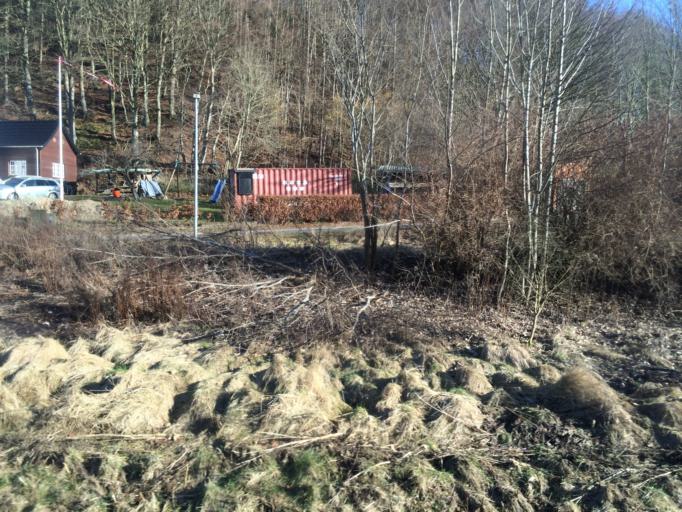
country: DK
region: South Denmark
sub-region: Vejle Kommune
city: Vejle
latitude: 55.7477
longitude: 9.5351
